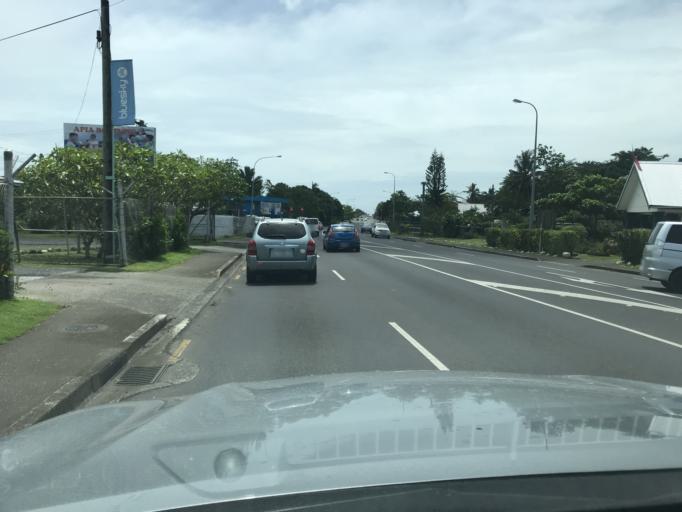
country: WS
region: Tuamasaga
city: Apia
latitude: -13.8384
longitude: -171.7726
